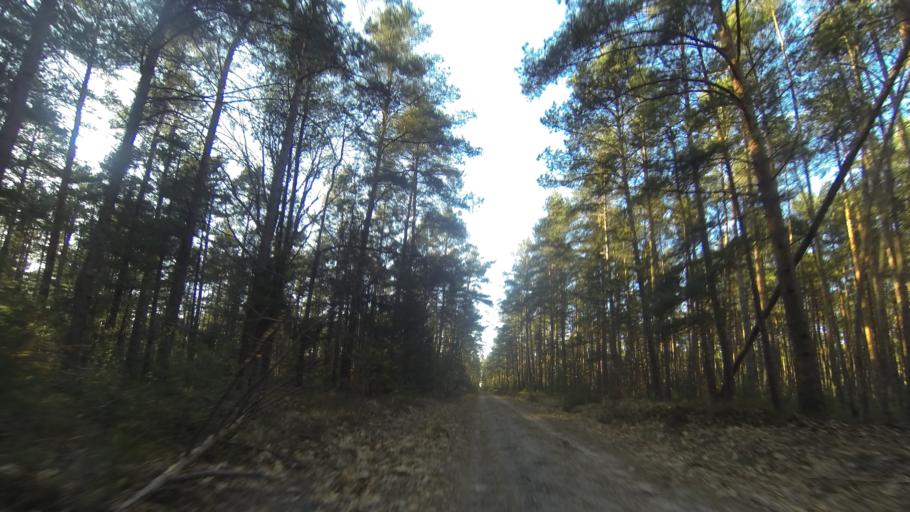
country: DE
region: Saxony
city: Tauscha
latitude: 51.2182
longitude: 13.7954
